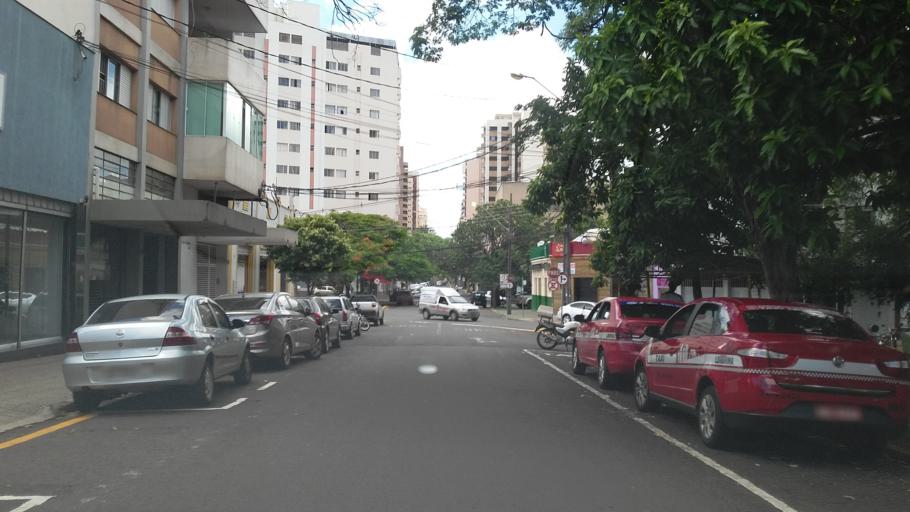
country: BR
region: Parana
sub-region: Londrina
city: Londrina
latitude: -23.3067
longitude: -51.1667
